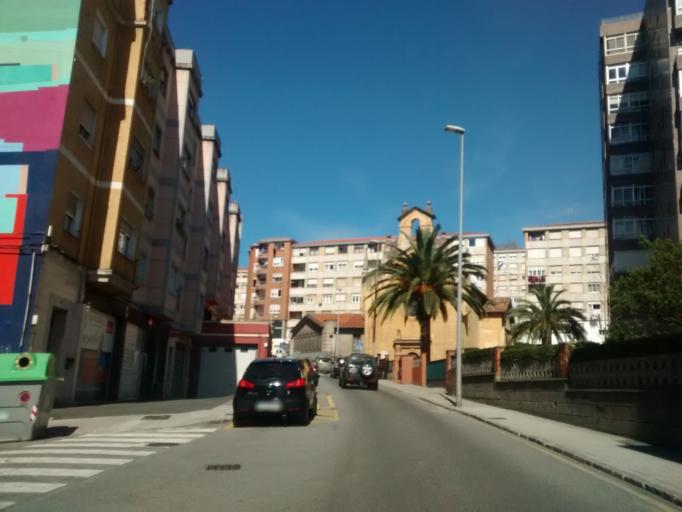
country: ES
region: Cantabria
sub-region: Provincia de Cantabria
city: Santander
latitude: 43.4639
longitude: -3.8149
